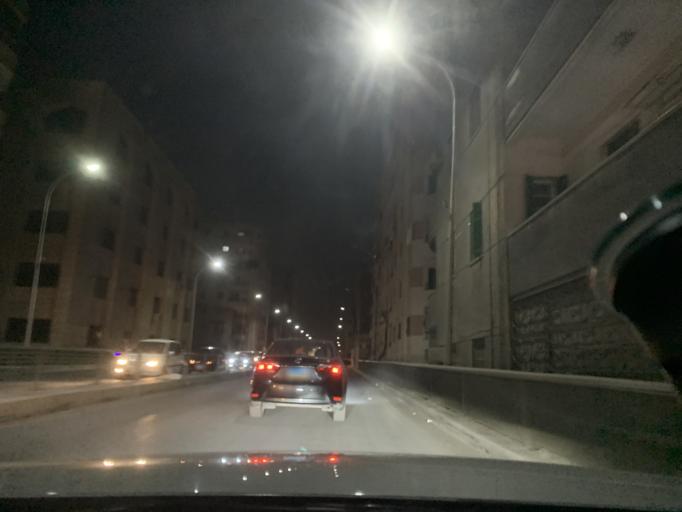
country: EG
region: Muhafazat al Qahirah
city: Cairo
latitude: 30.0861
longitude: 31.2936
